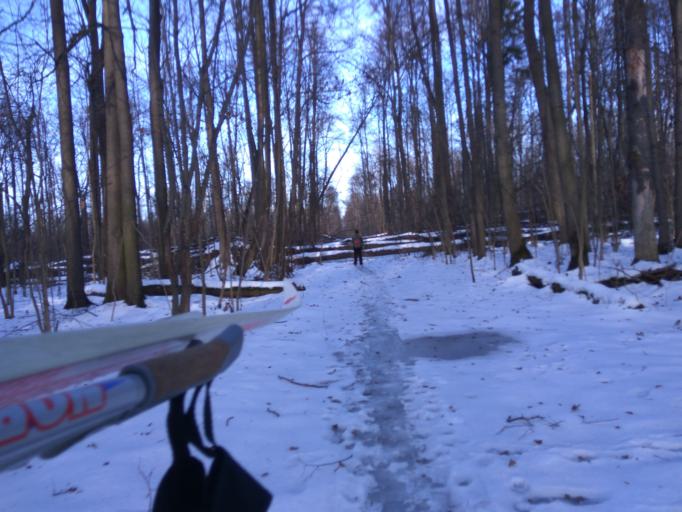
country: RU
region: Moscow
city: Babushkin
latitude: 55.8481
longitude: 37.7441
